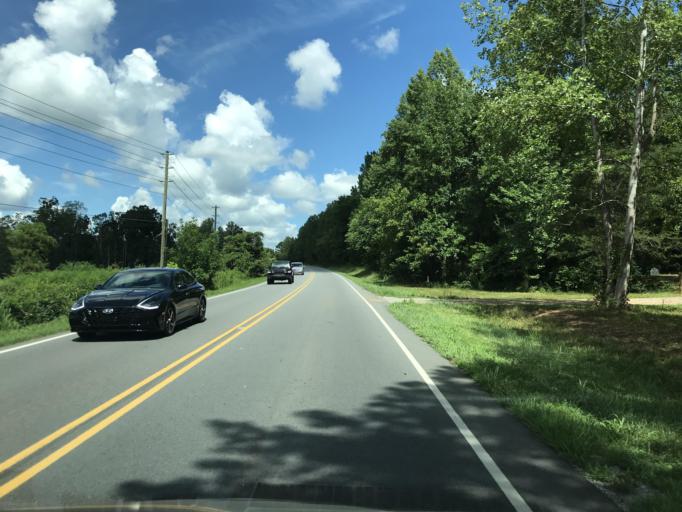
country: US
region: North Carolina
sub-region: Lincoln County
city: Pumpkin Center
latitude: 35.5096
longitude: -81.1594
